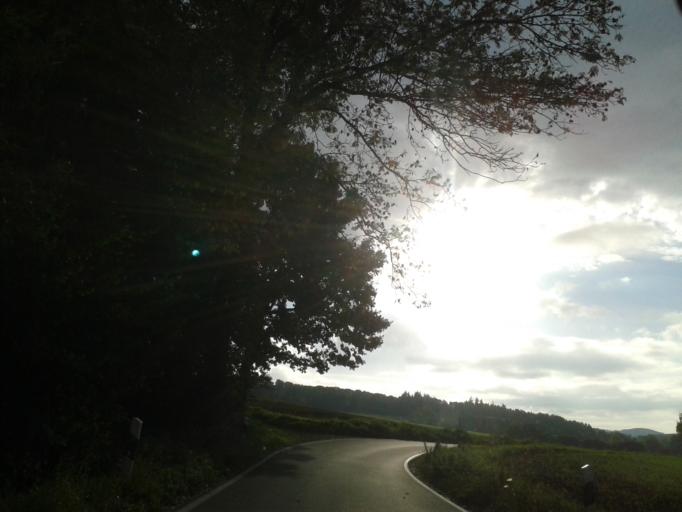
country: DE
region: North Rhine-Westphalia
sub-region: Regierungsbezirk Detmold
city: Lemgo
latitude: 52.0239
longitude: 8.9453
